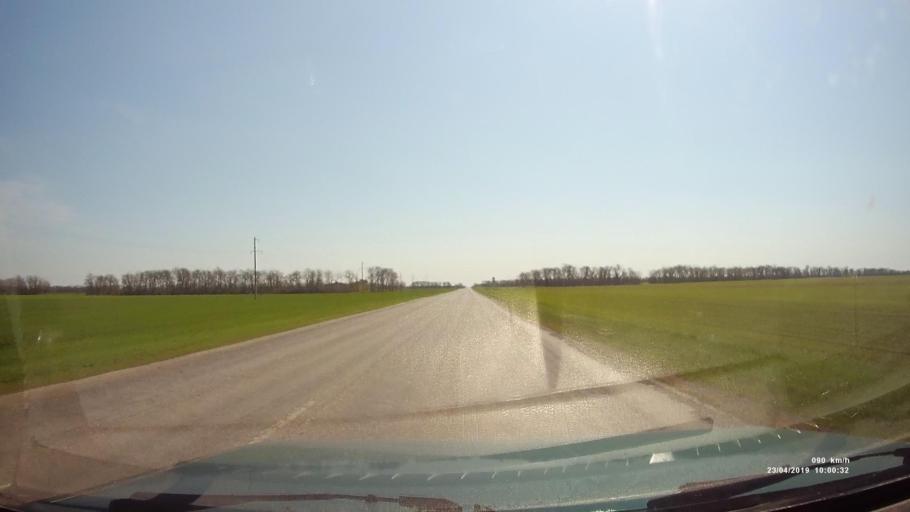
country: RU
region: Rostov
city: Sovetskoye
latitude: 46.7702
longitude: 42.1343
